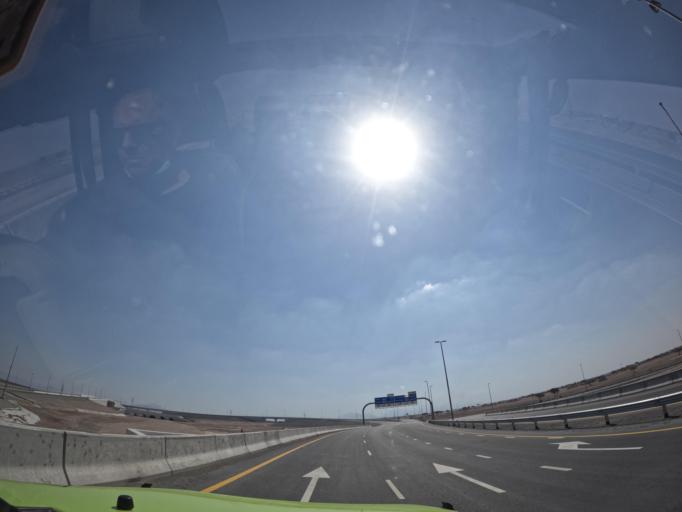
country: AE
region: Ash Shariqah
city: Adh Dhayd
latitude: 24.9106
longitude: 55.7965
